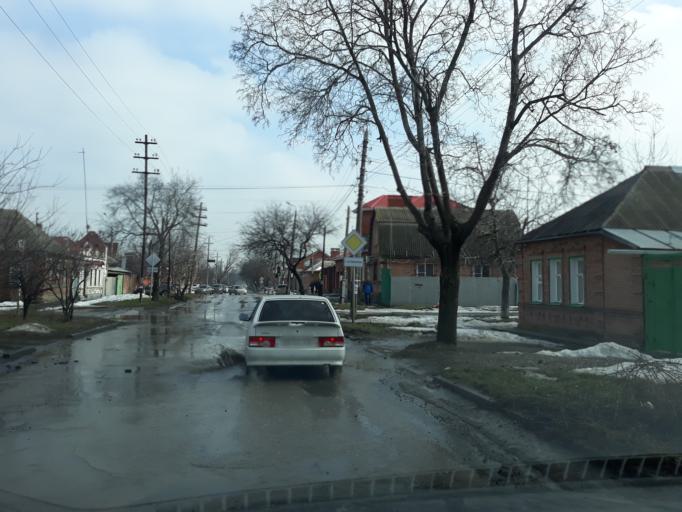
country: RU
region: Rostov
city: Taganrog
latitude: 47.2155
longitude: 38.8989
